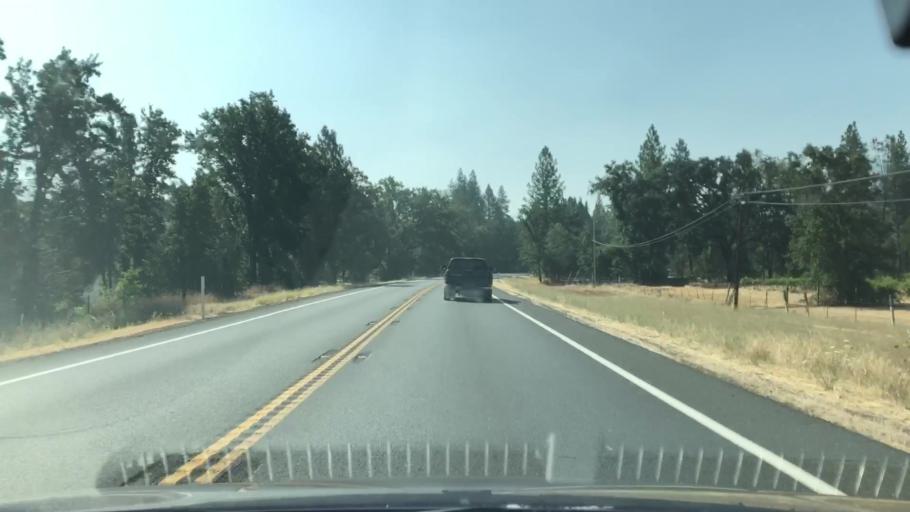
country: US
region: California
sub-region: Lake County
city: Middletown
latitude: 38.7276
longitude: -122.6201
